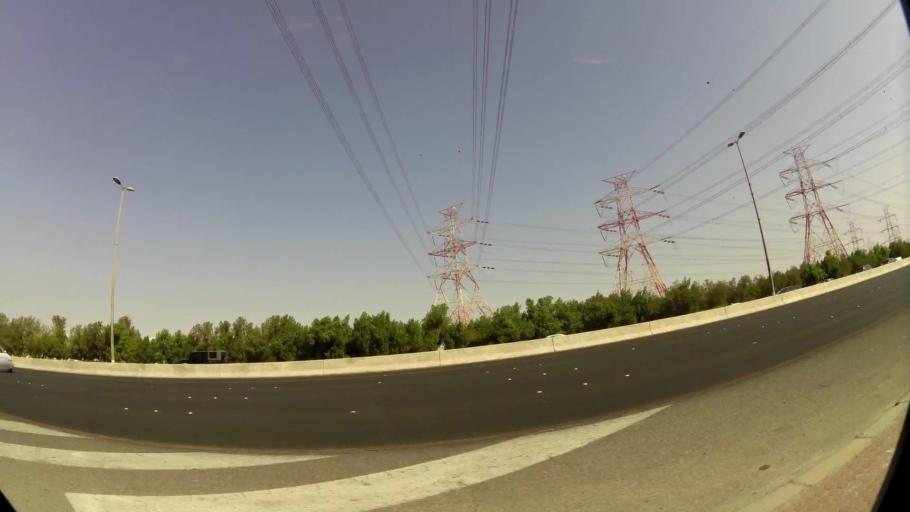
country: KW
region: Mubarak al Kabir
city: Sabah as Salim
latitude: 29.2706
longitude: 48.0394
